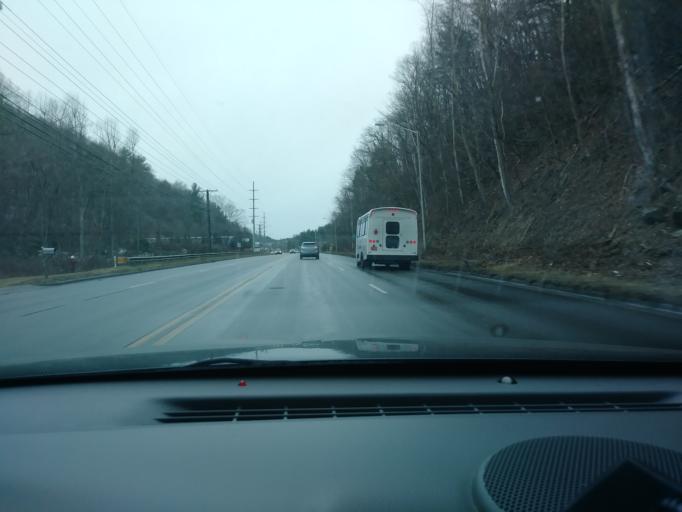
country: US
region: North Carolina
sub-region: Watauga County
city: Boone
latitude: 36.2032
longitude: -81.6877
